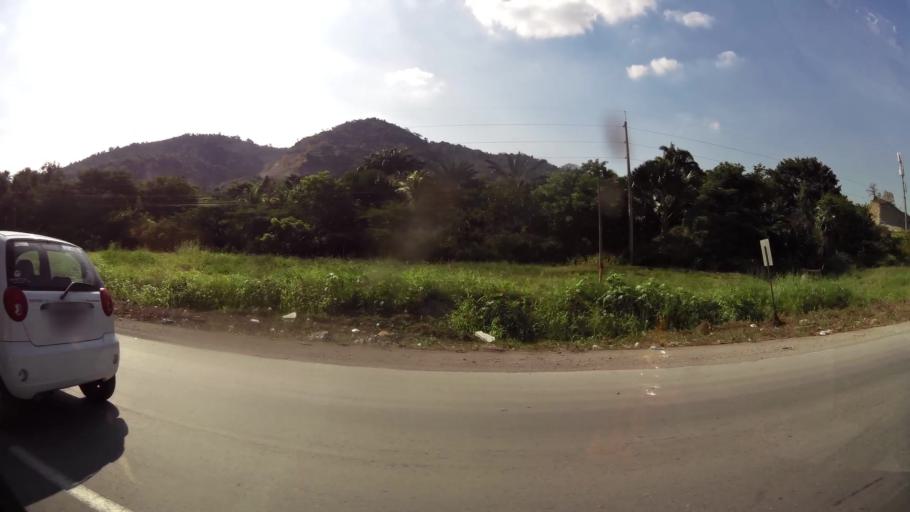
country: EC
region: Guayas
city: Santa Lucia
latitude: -2.1833
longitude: -79.9986
